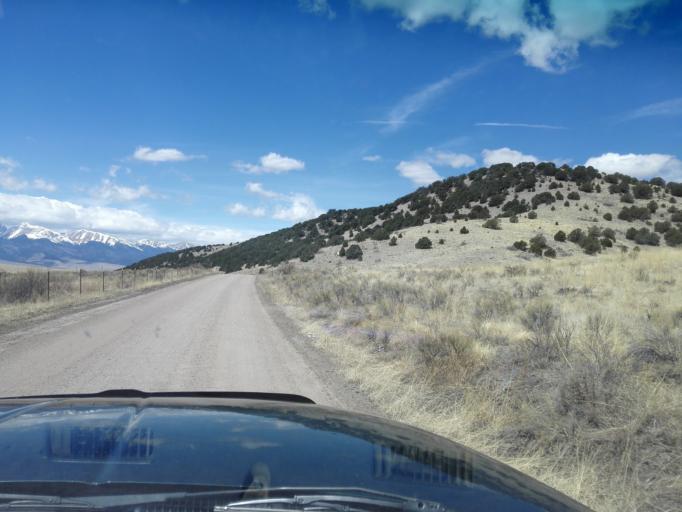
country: US
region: Colorado
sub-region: Custer County
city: Westcliffe
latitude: 37.9734
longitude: -105.2693
